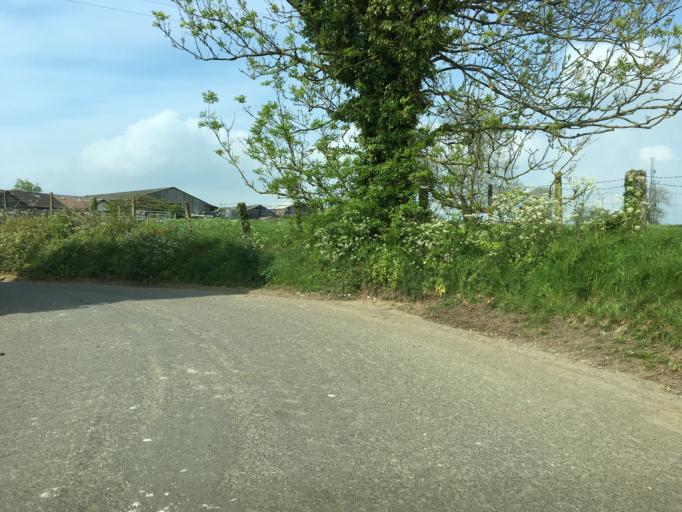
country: GB
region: England
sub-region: North Somerset
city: Dundry
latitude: 51.3989
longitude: -2.6401
